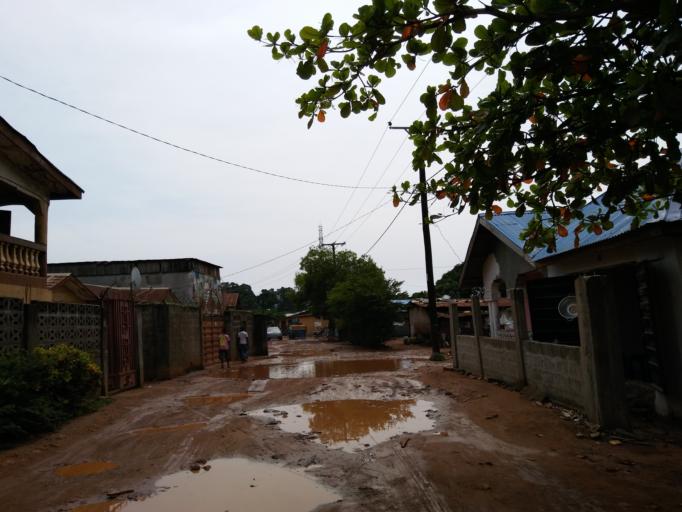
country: SL
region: Western Area
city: Hastings
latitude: 8.3838
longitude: -13.1471
